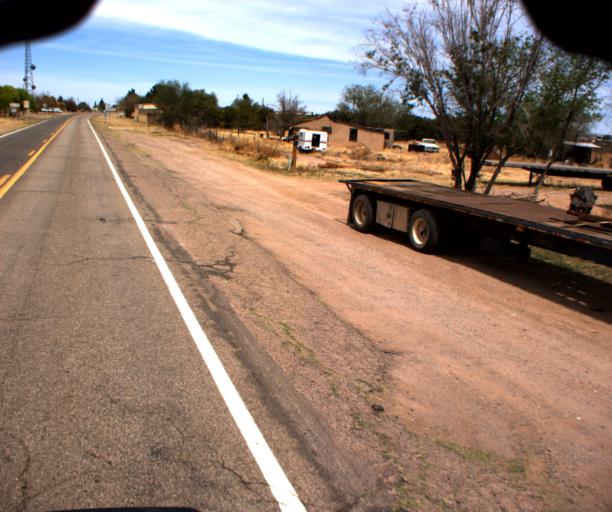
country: US
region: Arizona
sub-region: Cochise County
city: Bisbee
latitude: 31.6770
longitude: -109.6855
